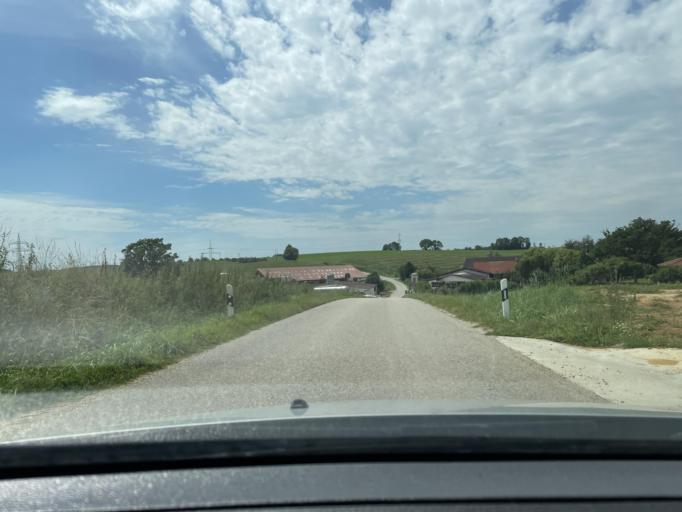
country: DE
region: Bavaria
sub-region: Lower Bavaria
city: Geisenhausen
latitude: 48.4420
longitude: 12.2950
